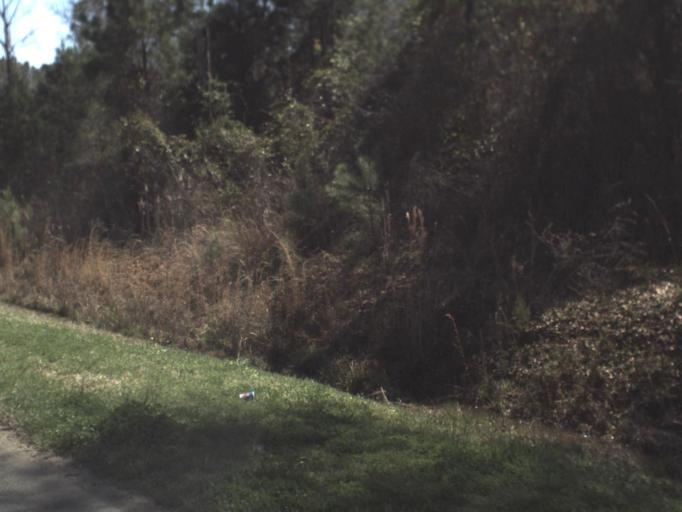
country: US
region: Florida
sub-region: Jackson County
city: Marianna
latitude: 30.8034
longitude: -85.2803
